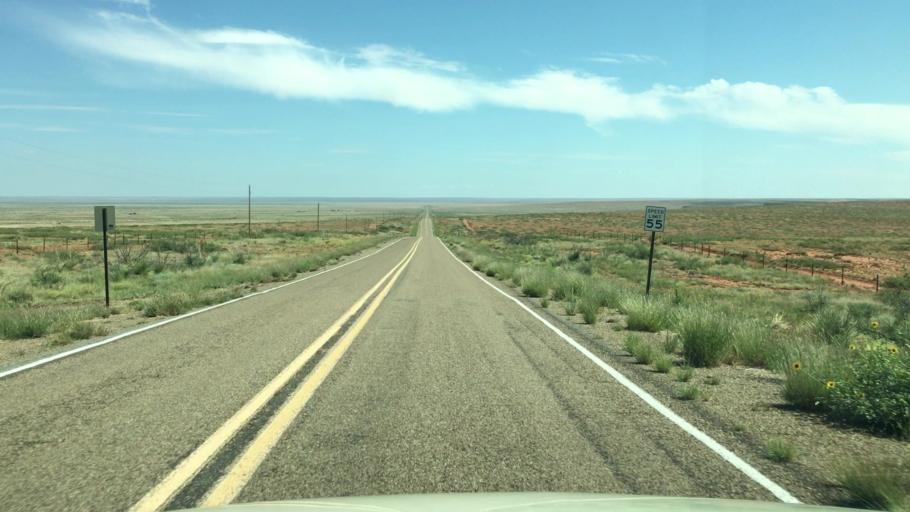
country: US
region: New Mexico
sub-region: Chaves County
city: Roswell
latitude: 33.9691
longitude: -104.5800
